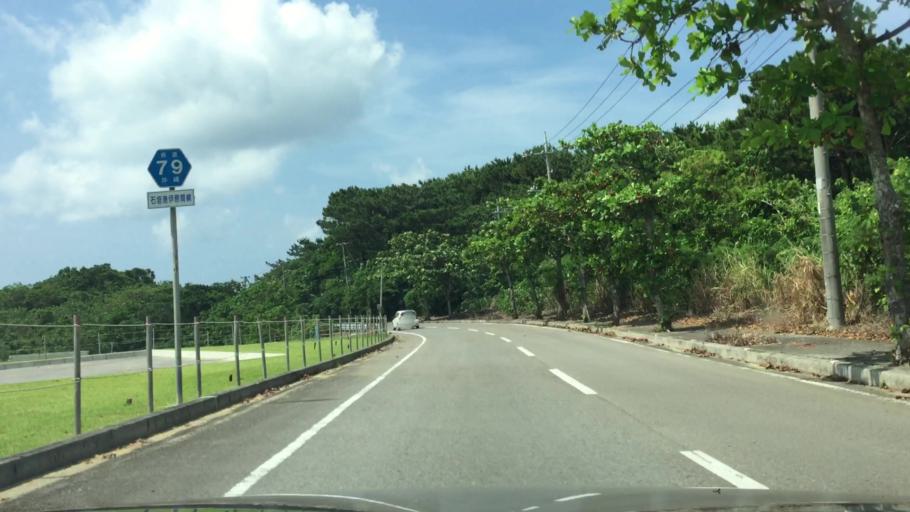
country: JP
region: Okinawa
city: Ishigaki
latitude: 24.4709
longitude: 124.2244
